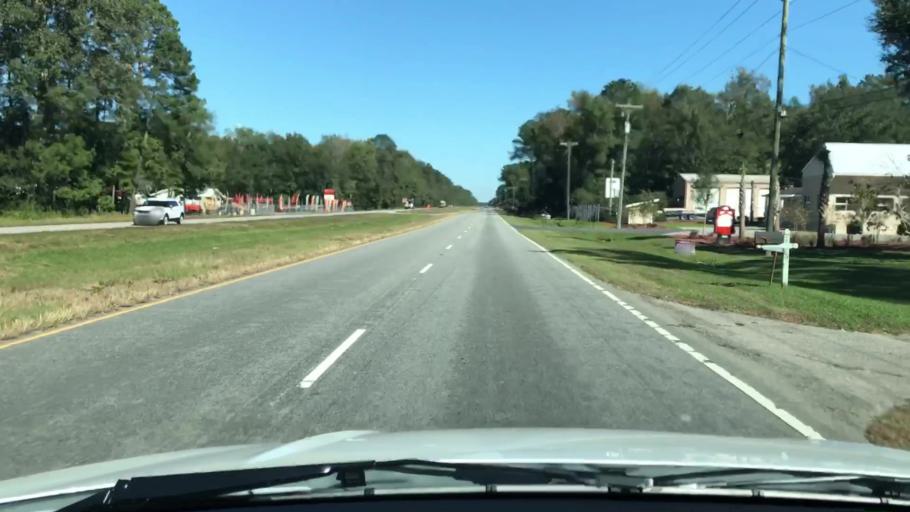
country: US
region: South Carolina
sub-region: Charleston County
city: Ravenel
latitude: 32.7564
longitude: -80.3244
